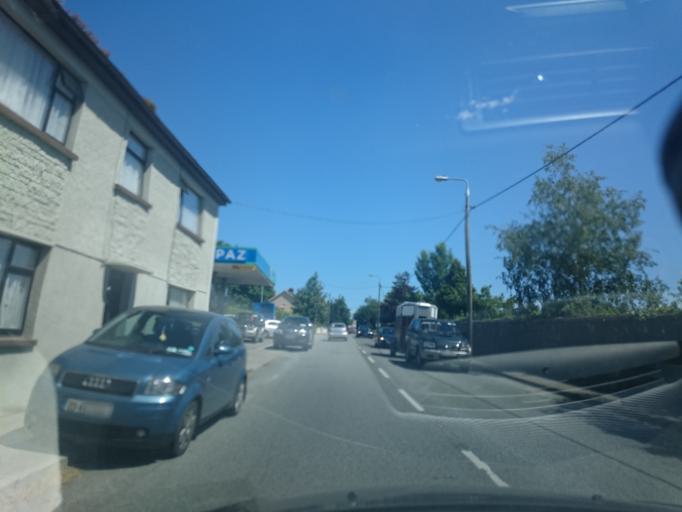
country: IE
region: Leinster
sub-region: County Carlow
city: Bagenalstown
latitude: 52.6305
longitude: -7.0619
